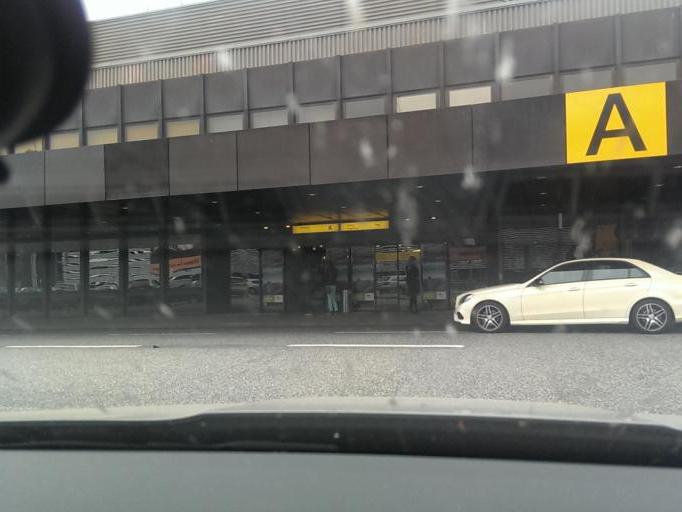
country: DE
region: Lower Saxony
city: Langenhagen
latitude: 52.4597
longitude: 9.6947
